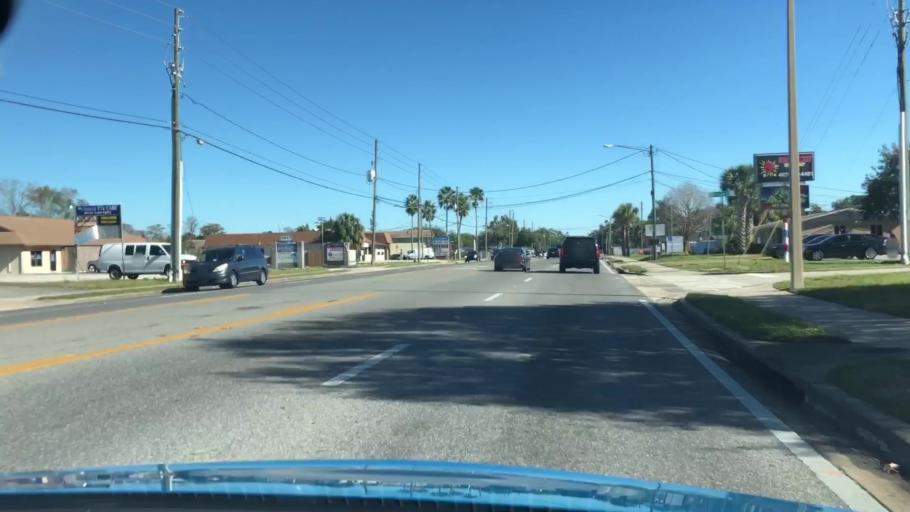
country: US
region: Florida
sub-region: Orange County
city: Sky Lake
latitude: 28.4725
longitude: -81.3942
